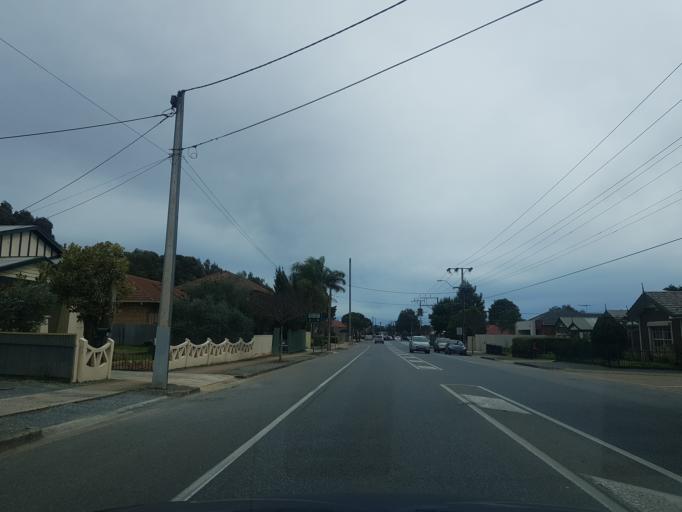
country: AU
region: South Australia
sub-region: Campbelltown
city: Paradise
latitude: -34.8696
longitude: 138.6786
